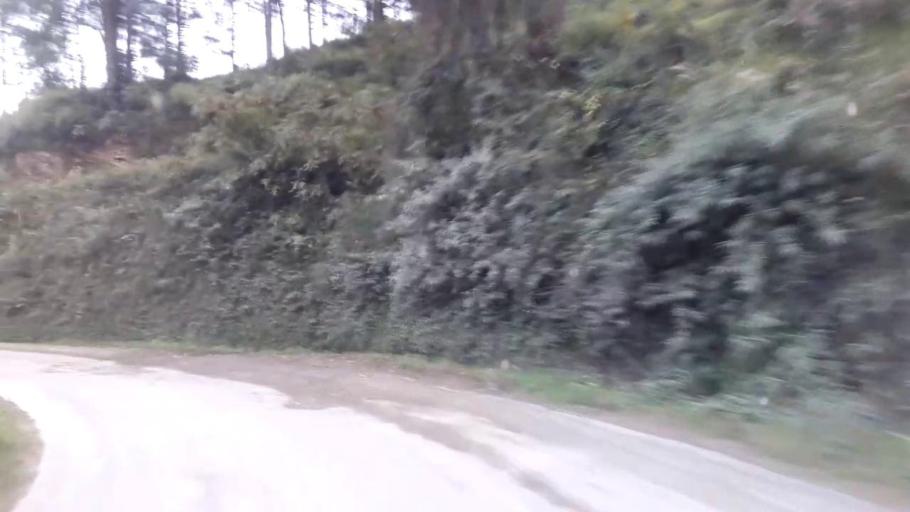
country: IN
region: Himachal Pradesh
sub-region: Shimla
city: Shimla
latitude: 31.0661
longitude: 77.1479
